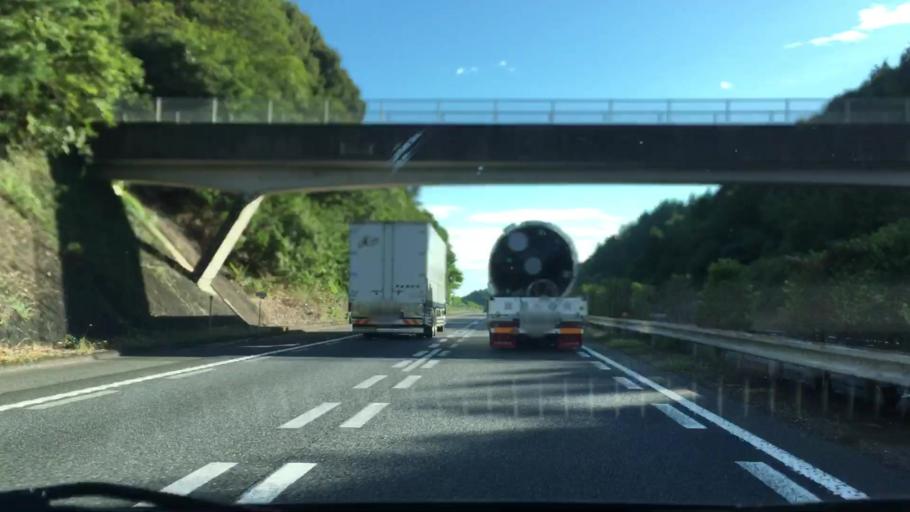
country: JP
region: Yamaguchi
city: Hikari
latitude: 34.0550
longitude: 132.0037
